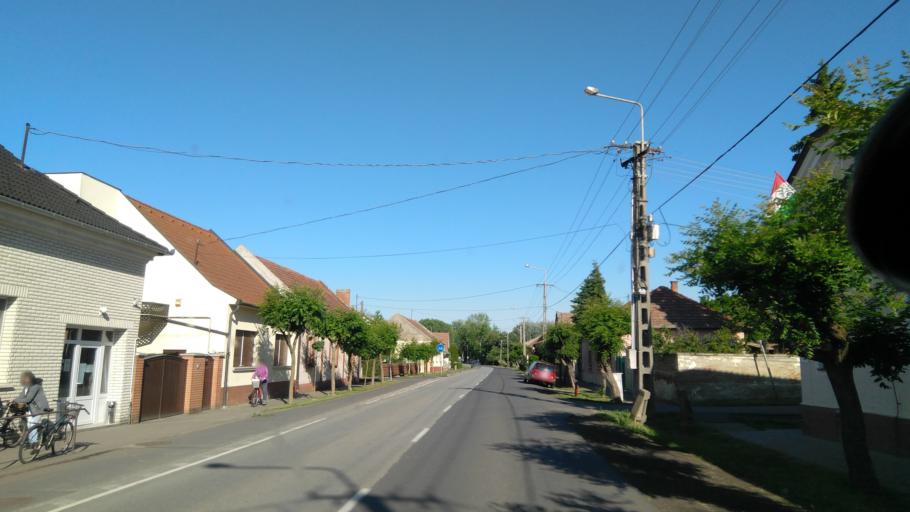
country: HU
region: Bekes
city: Elek
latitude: 46.5307
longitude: 21.2485
